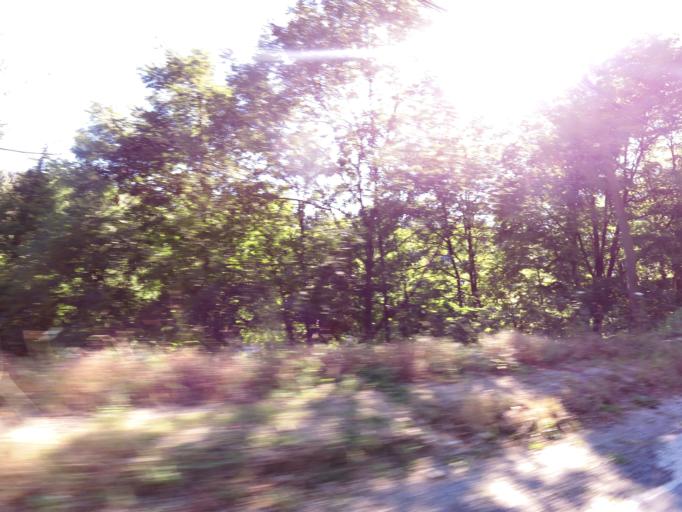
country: FR
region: Languedoc-Roussillon
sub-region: Departement du Gard
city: Saint-Jean-du-Gard
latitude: 44.1141
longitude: 3.8543
